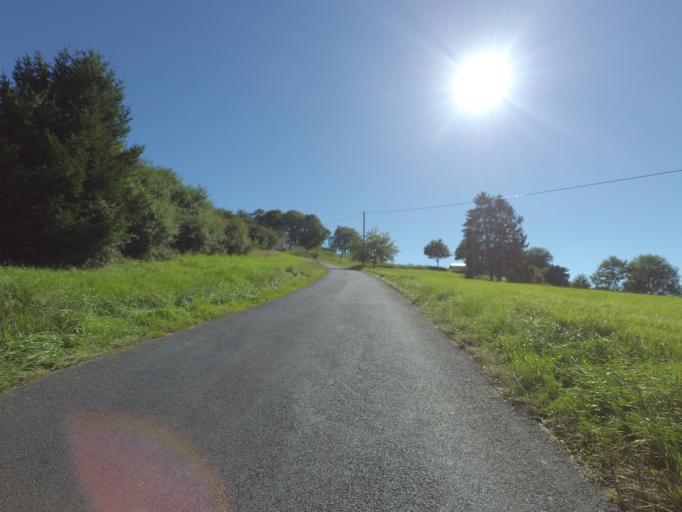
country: DE
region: Rheinland-Pfalz
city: Boxberg
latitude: 50.2575
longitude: 6.8805
